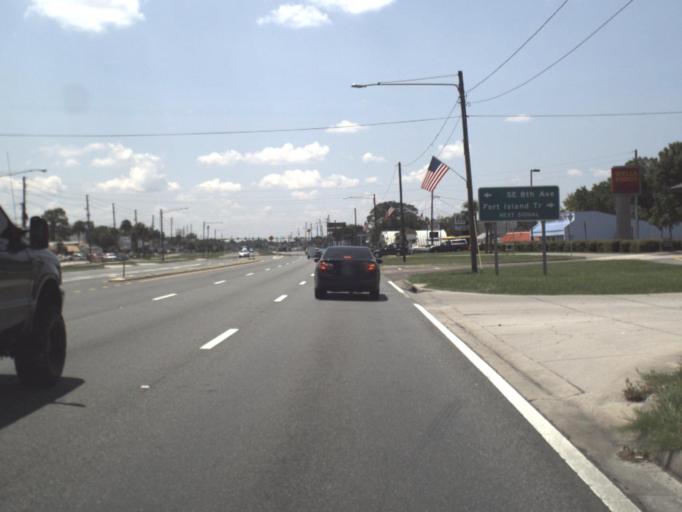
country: US
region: Florida
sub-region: Citrus County
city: Crystal River
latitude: 28.8868
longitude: -82.5842
